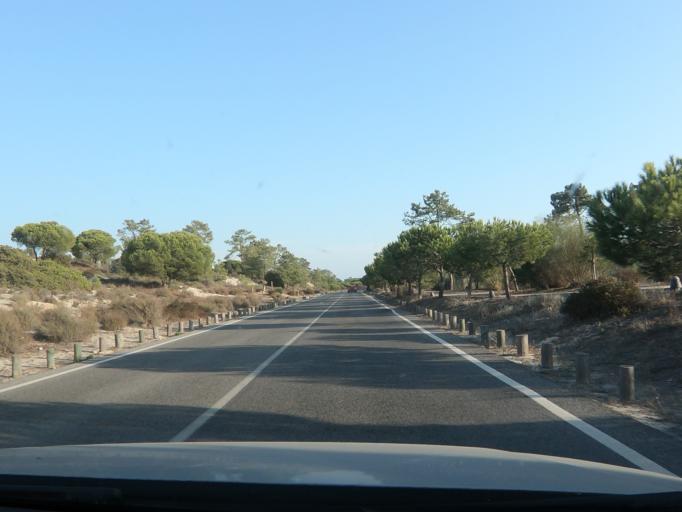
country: PT
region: Setubal
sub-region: Setubal
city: Setubal
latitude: 38.4775
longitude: -8.8880
